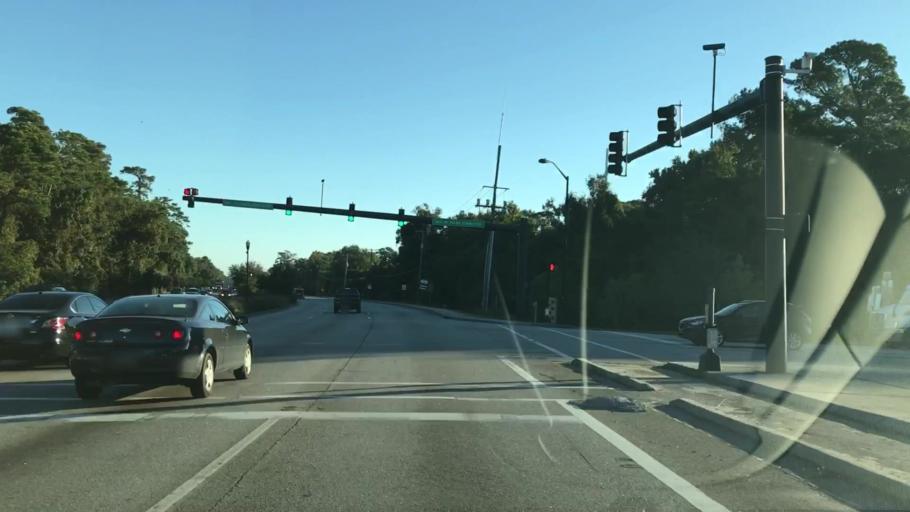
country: US
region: South Carolina
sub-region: Charleston County
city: Mount Pleasant
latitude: 32.8334
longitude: -79.8260
